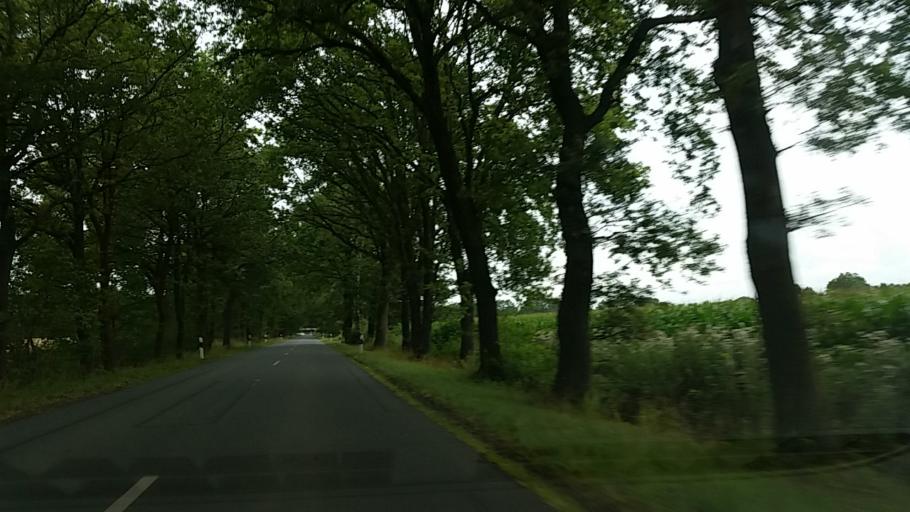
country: DE
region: Lower Saxony
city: Hipstedt
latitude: 53.4223
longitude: 8.9063
